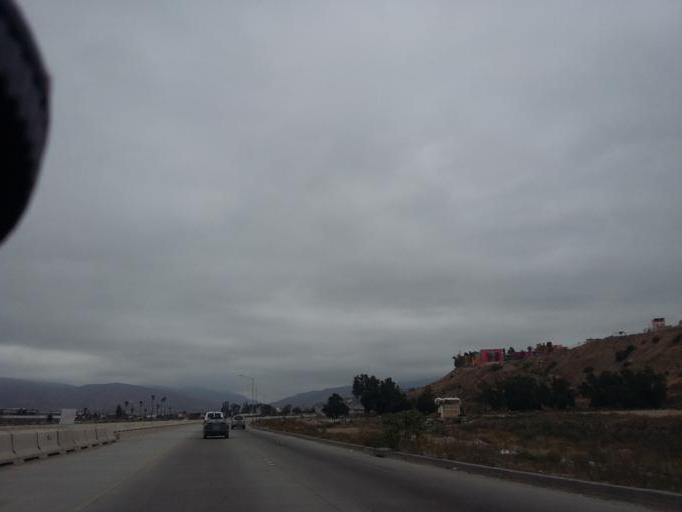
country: MX
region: Baja California
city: Tijuana
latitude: 32.5126
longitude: -116.9374
